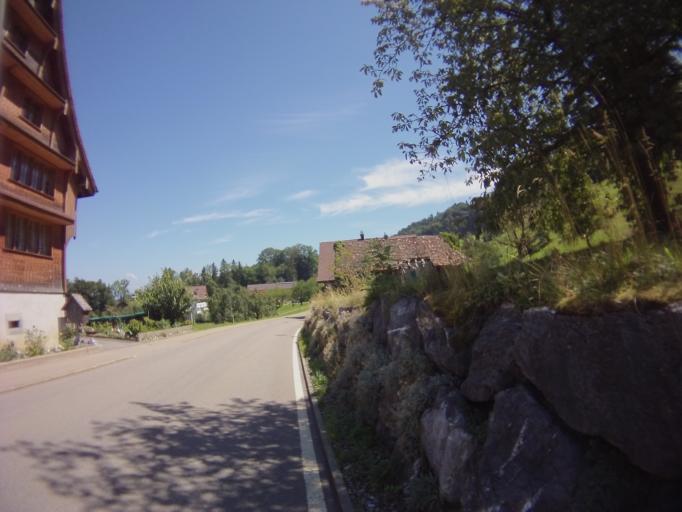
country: CH
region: Schwyz
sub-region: Bezirk Hoefe
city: Feusisberg
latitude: 47.1885
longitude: 8.7583
